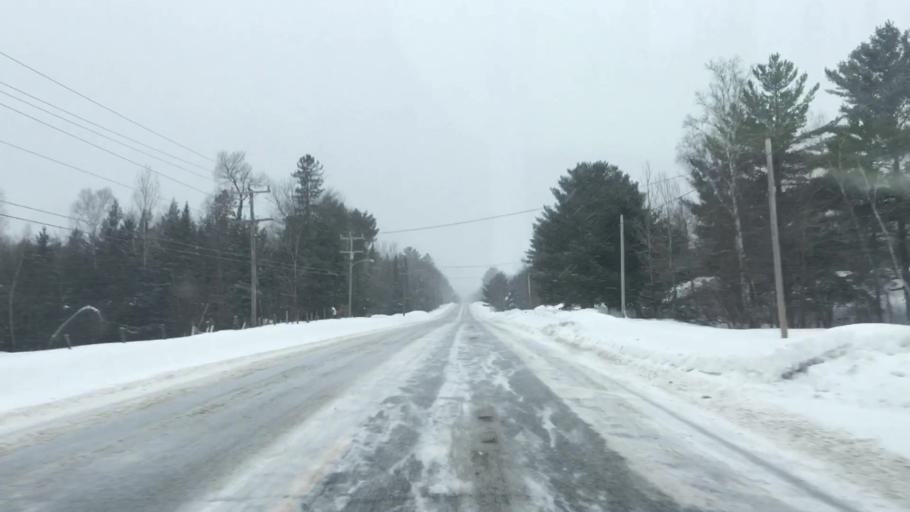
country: US
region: Maine
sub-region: Penobscot County
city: Medway
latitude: 45.5454
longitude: -68.3727
